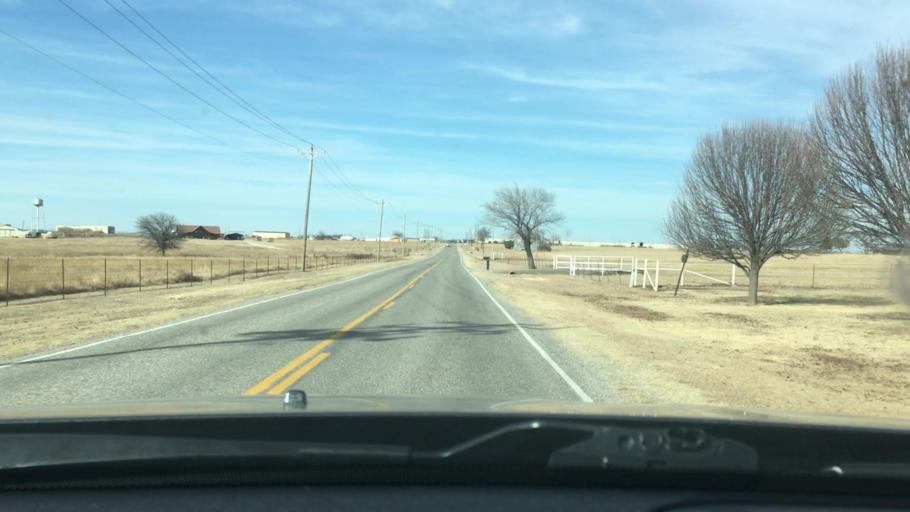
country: US
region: Oklahoma
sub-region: Murray County
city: Davis
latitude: 34.4986
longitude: -97.0904
